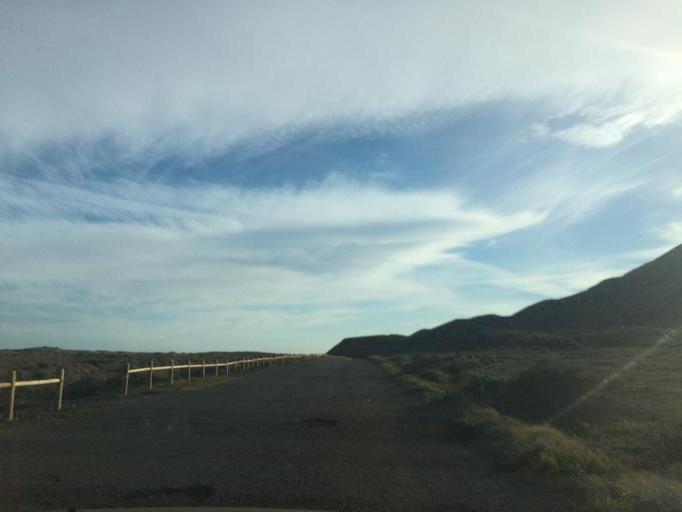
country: ES
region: Andalusia
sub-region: Provincia de Almeria
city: San Jose
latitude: 36.7993
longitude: -2.0637
